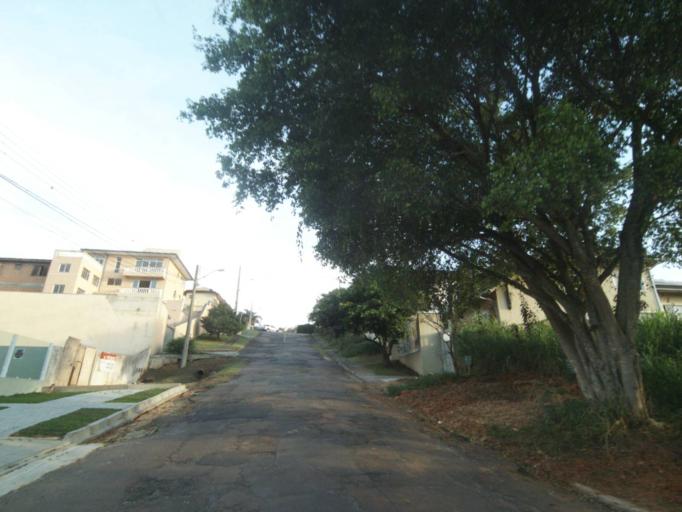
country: BR
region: Parana
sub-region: Curitiba
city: Curitiba
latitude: -25.4557
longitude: -49.3117
